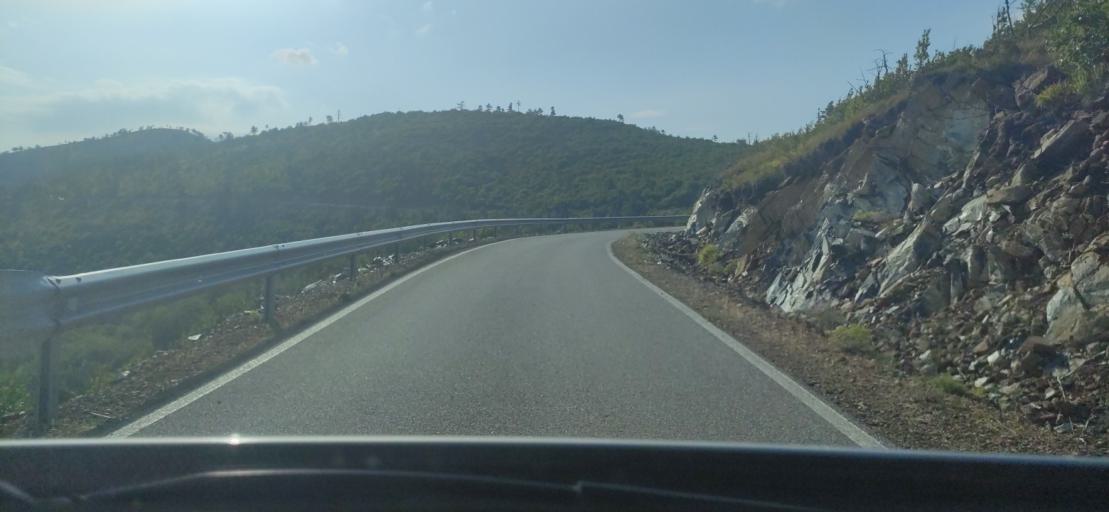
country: AL
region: Shkoder
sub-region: Rrethi i Pukes
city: Iballe
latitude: 42.1713
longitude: 20.0069
